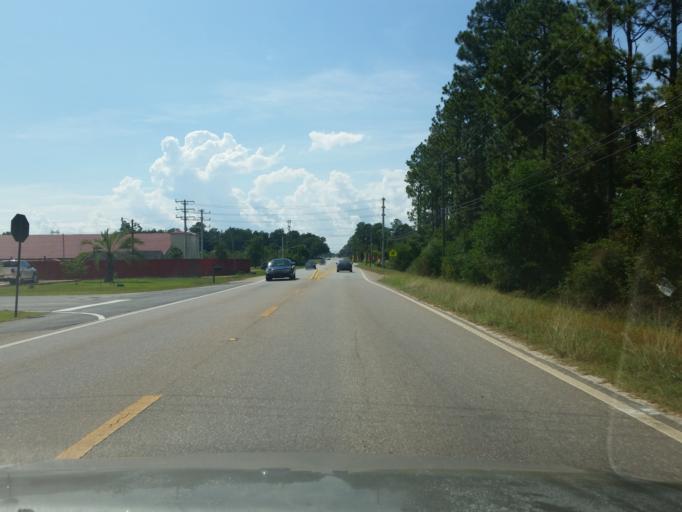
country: US
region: Alabama
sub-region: Baldwin County
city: Spanish Fort
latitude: 30.6768
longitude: -87.8419
